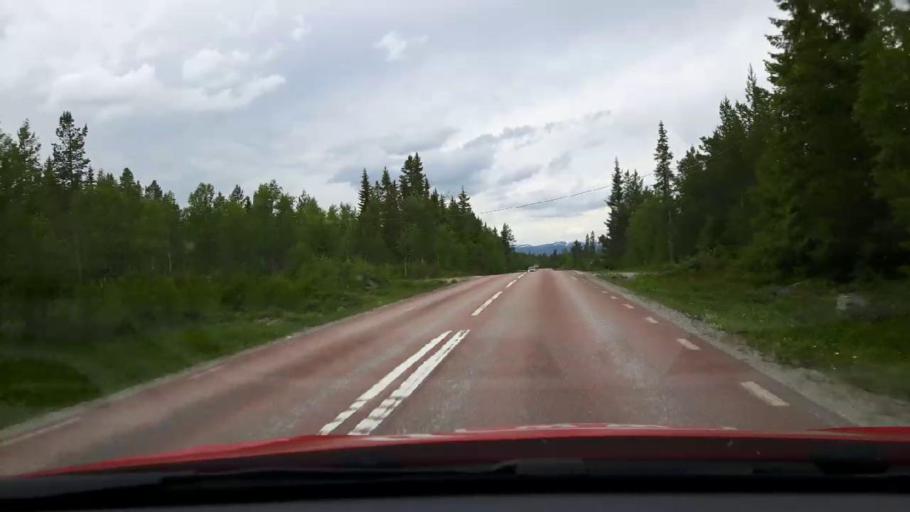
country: NO
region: Hedmark
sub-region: Engerdal
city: Engerdal
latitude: 62.5060
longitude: 12.6167
